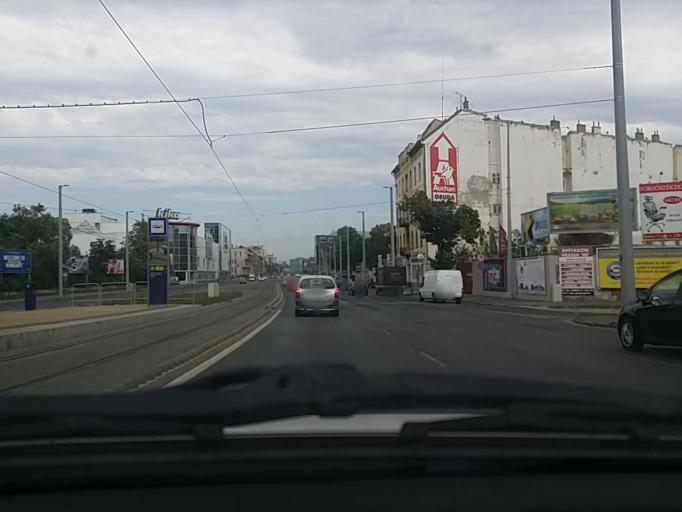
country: HU
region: Budapest
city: Budapest XIII. keruelet
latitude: 47.5235
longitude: 19.0813
